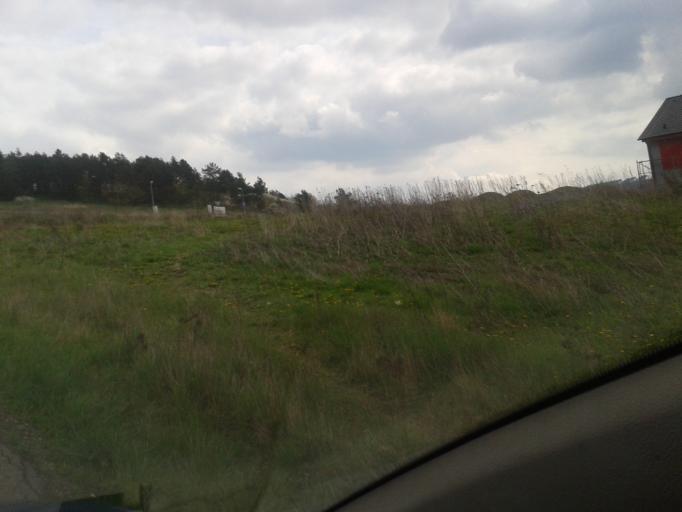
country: CZ
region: Central Bohemia
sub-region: Okres Beroun
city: Kraluv Dvur
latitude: 49.9546
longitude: 14.0334
